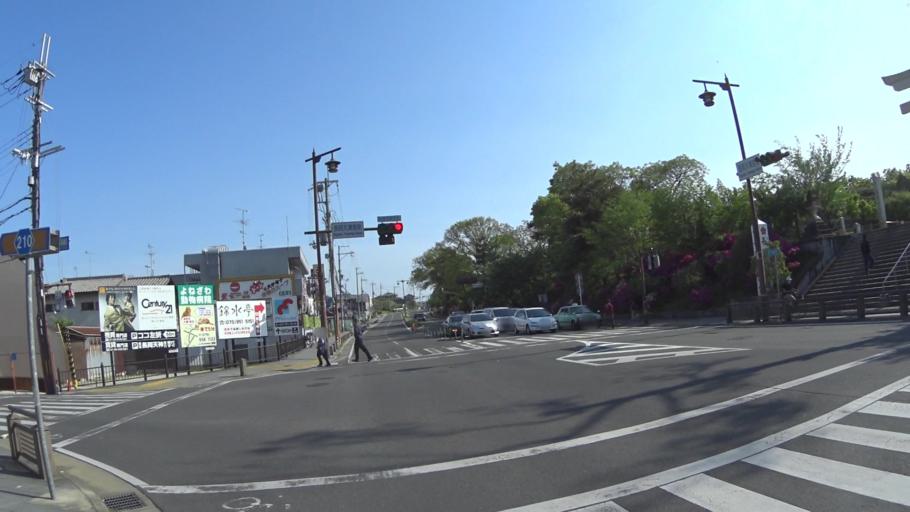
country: JP
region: Kyoto
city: Muko
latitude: 34.9240
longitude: 135.6890
